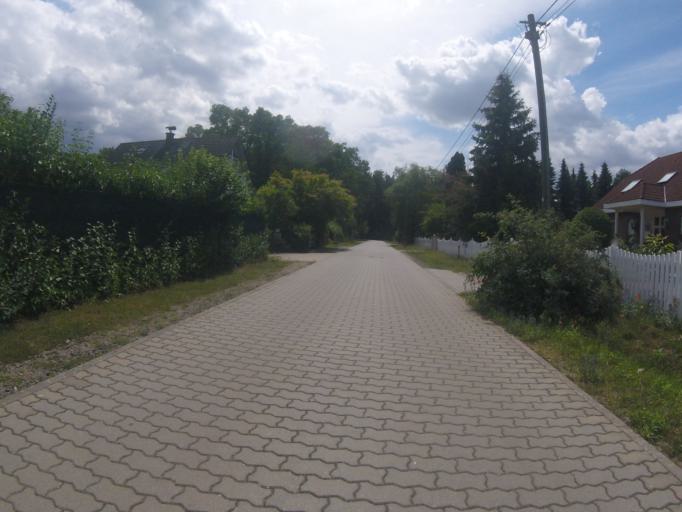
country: DE
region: Brandenburg
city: Bestensee
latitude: 52.2502
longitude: 13.6378
